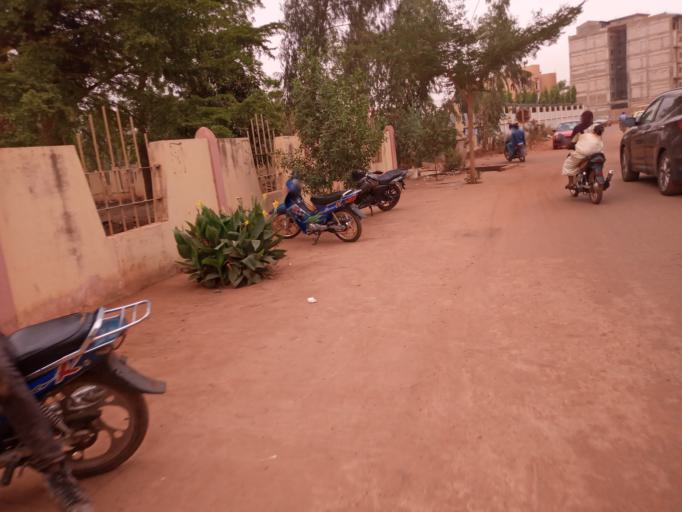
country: ML
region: Bamako
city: Bamako
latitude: 12.6376
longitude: -8.0216
